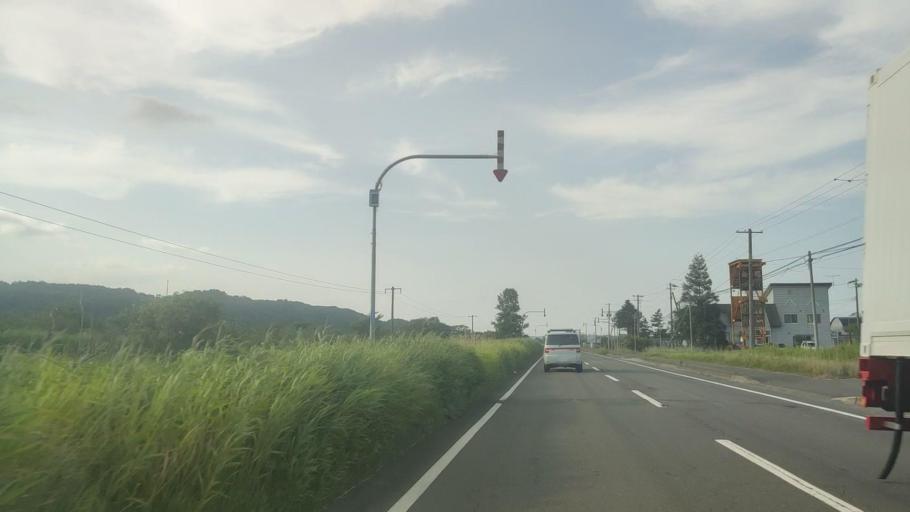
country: JP
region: Hokkaido
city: Iwamizawa
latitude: 42.9888
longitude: 141.7915
